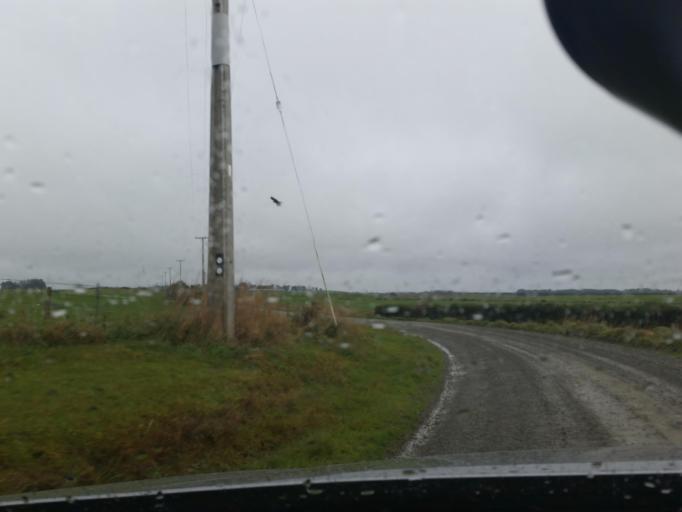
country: NZ
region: Southland
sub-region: Southland District
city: Winton
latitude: -46.1859
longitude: 168.2284
